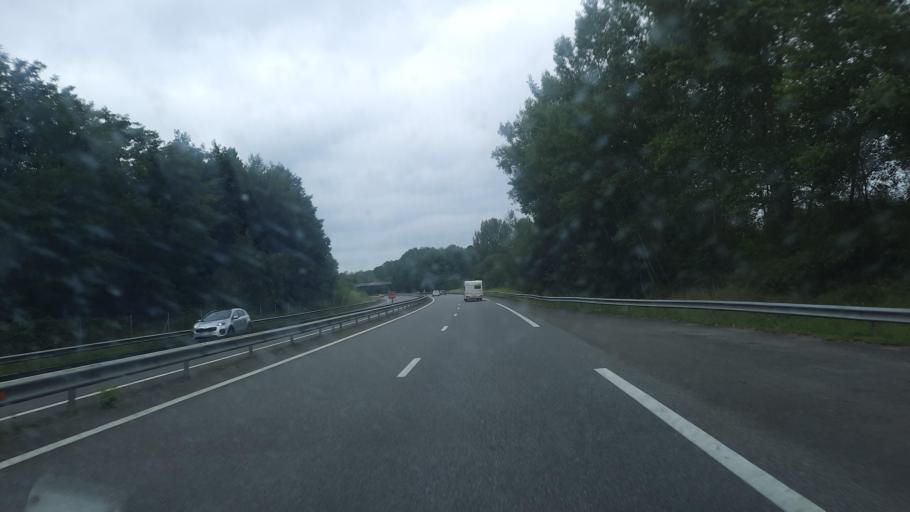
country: FR
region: Midi-Pyrenees
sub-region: Departement des Hautes-Pyrenees
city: Barbazan-Debat
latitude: 43.2001
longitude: 0.1759
